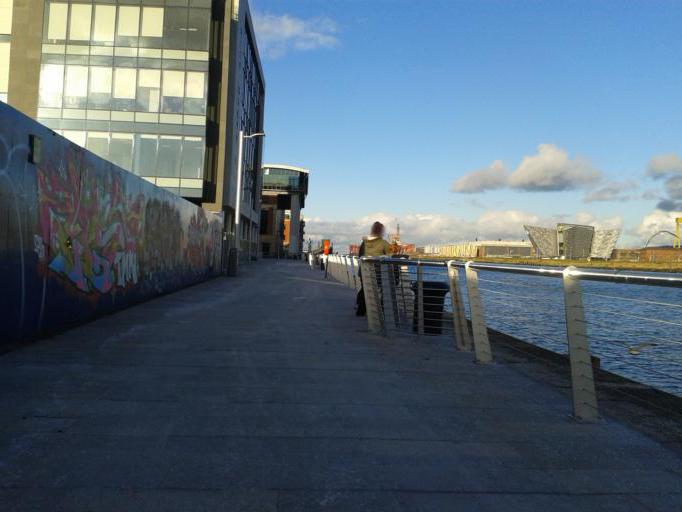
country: GB
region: Northern Ireland
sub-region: City of Belfast
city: Belfast
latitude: 54.6049
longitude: -5.9196
